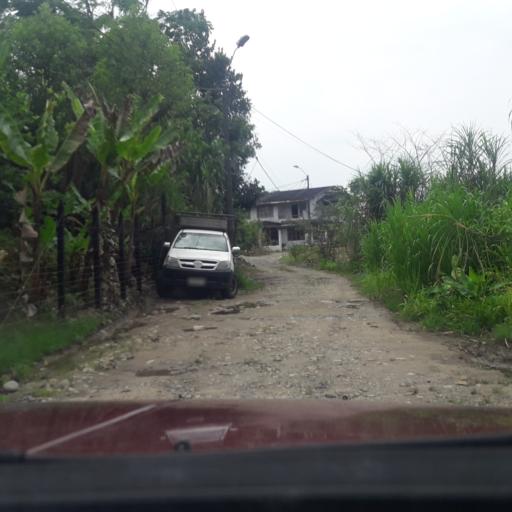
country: EC
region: Napo
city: Tena
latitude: -0.9828
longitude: -77.8148
